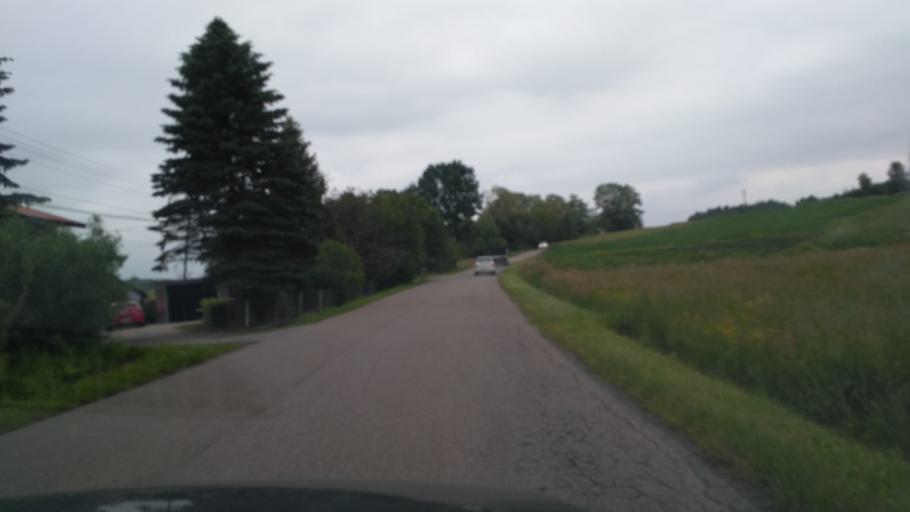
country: PL
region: Subcarpathian Voivodeship
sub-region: Powiat kolbuszowski
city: Niwiska
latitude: 50.1590
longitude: 21.6672
